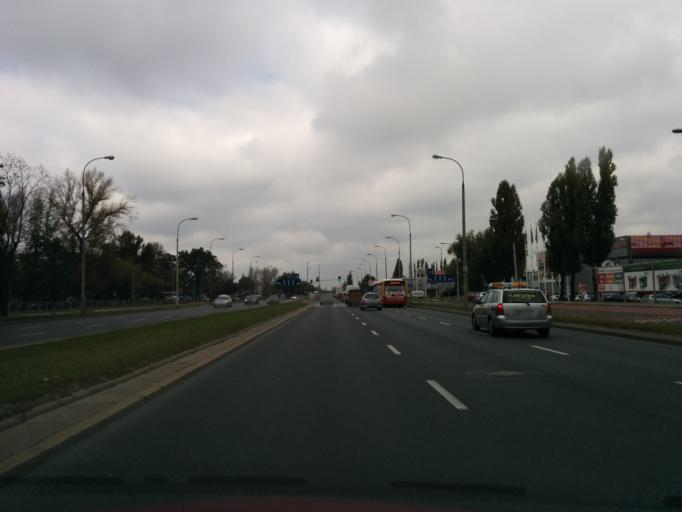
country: PL
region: Masovian Voivodeship
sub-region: Warszawa
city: Praga Polnoc
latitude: 52.2727
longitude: 21.0156
